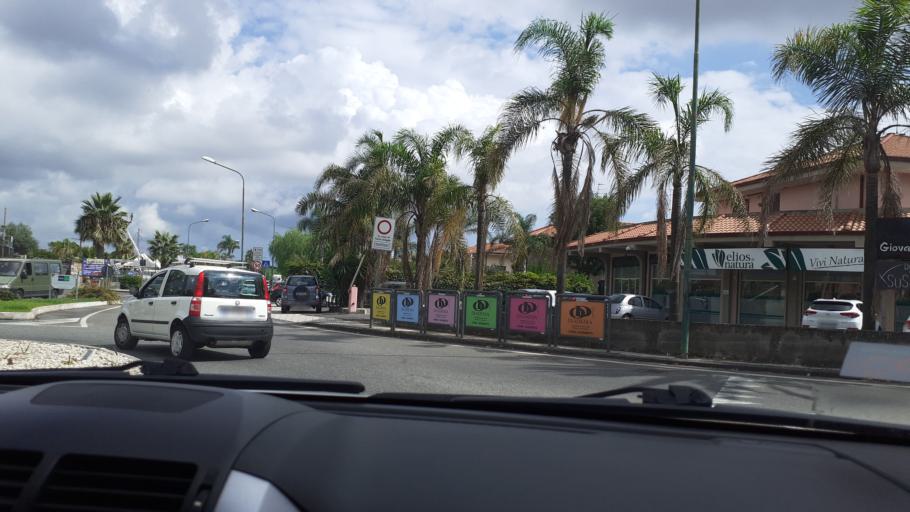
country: IT
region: Sicily
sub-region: Catania
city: San Gregorio di Catania
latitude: 37.5676
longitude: 15.1064
